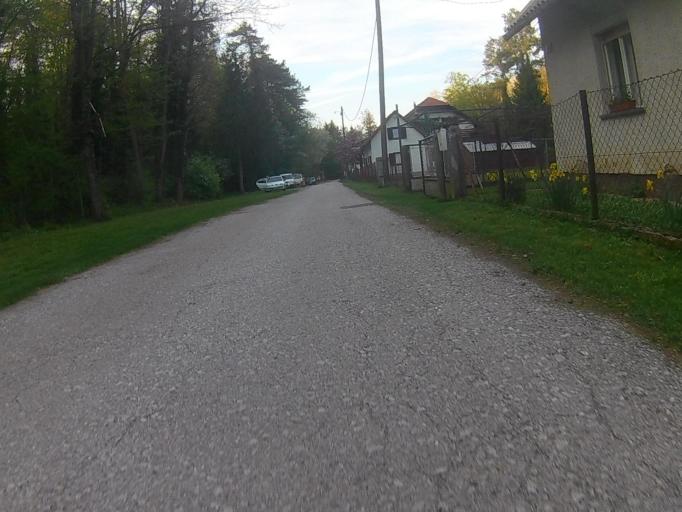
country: SI
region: Maribor
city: Kamnica
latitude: 46.5619
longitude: 15.6104
